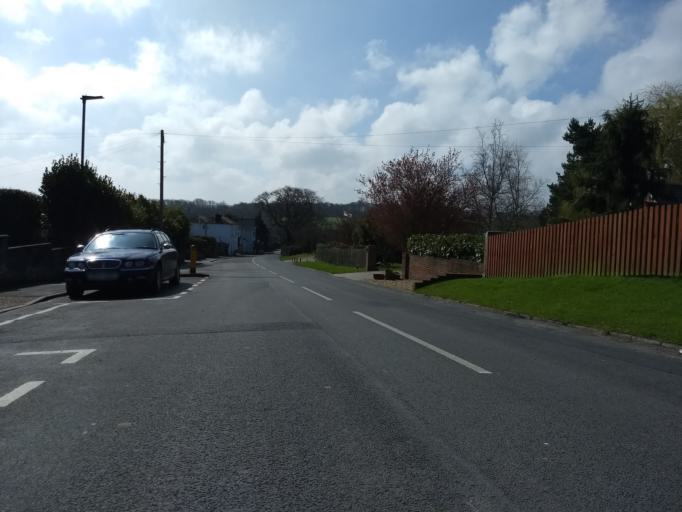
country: GB
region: England
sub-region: Isle of Wight
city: Ryde
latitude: 50.7167
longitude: -1.1663
